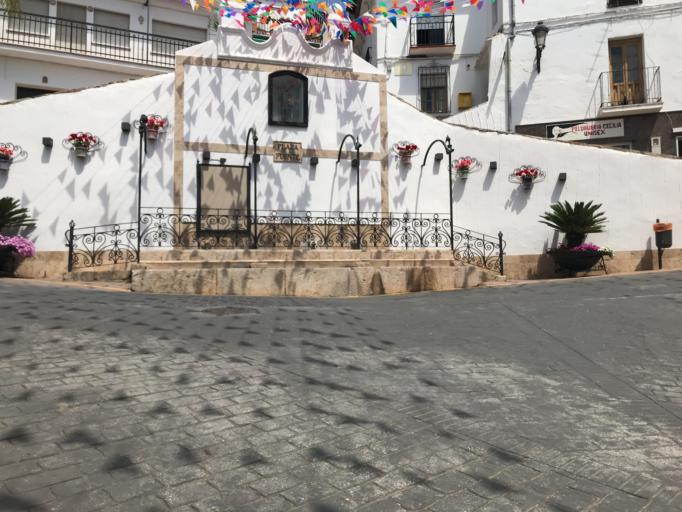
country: ES
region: Andalusia
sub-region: Provincia de Malaga
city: Periana
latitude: 36.9280
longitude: -4.1917
